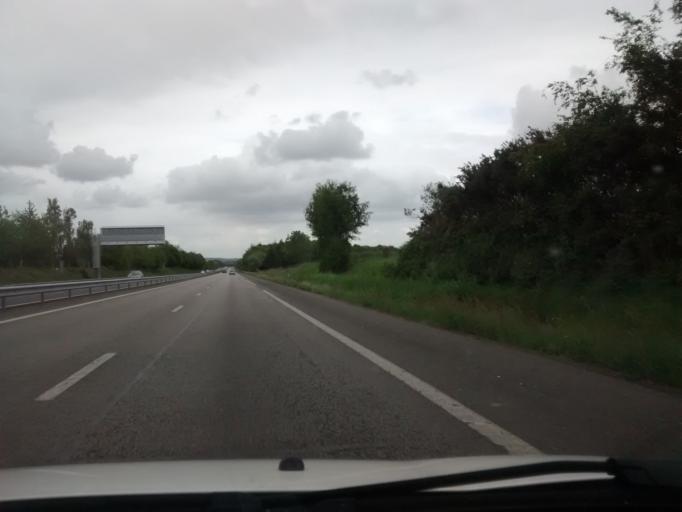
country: FR
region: Brittany
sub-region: Departement du Morbihan
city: Campeneac
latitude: 47.9252
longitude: -2.3358
